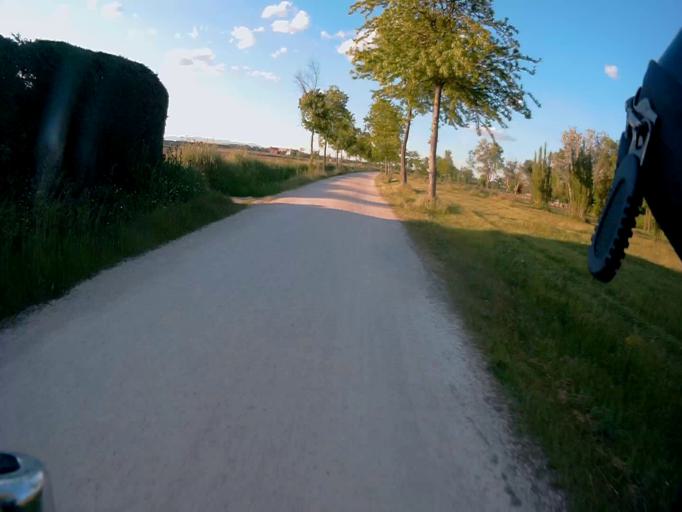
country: ES
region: Madrid
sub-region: Provincia de Madrid
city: Alcorcon
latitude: 40.3290
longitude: -3.8046
